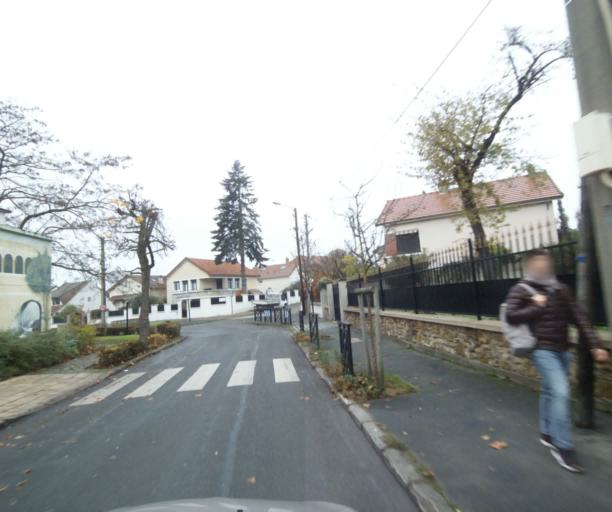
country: FR
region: Ile-de-France
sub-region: Departement de Seine-Saint-Denis
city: Gagny
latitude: 48.8756
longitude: 2.5442
